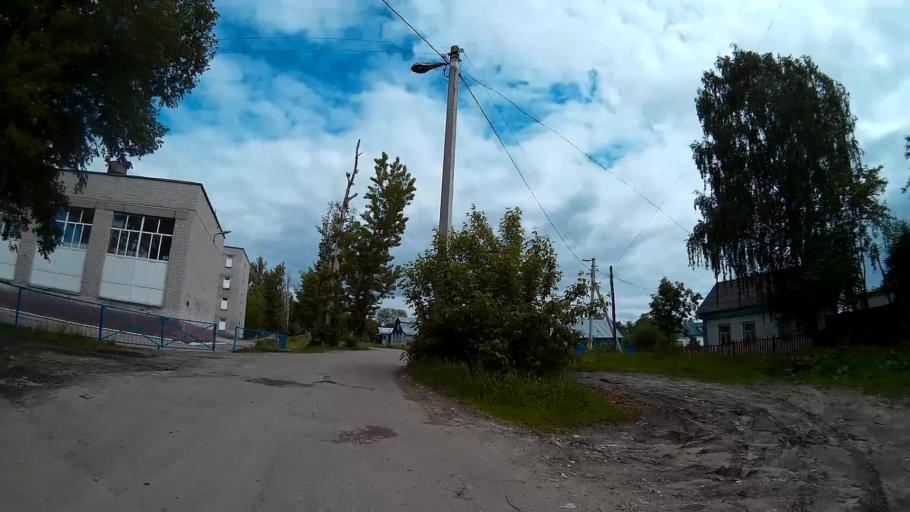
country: RU
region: Ulyanovsk
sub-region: Ulyanovskiy Rayon
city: Ulyanovsk
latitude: 54.2521
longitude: 48.3035
